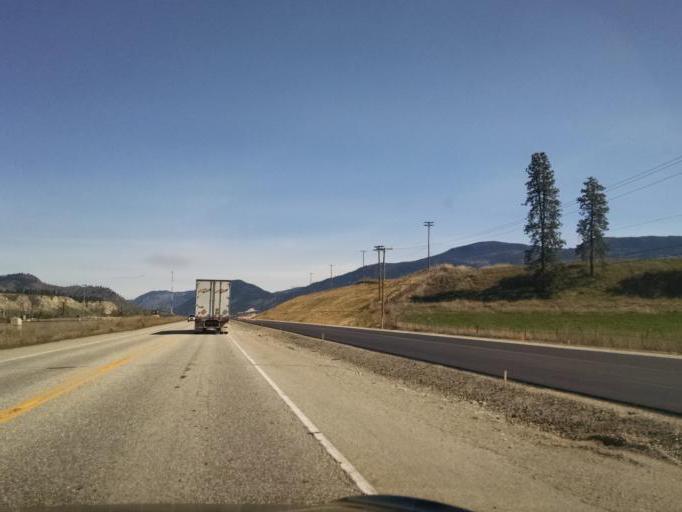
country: CA
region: British Columbia
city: Chase
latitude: 50.6653
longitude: -119.8603
